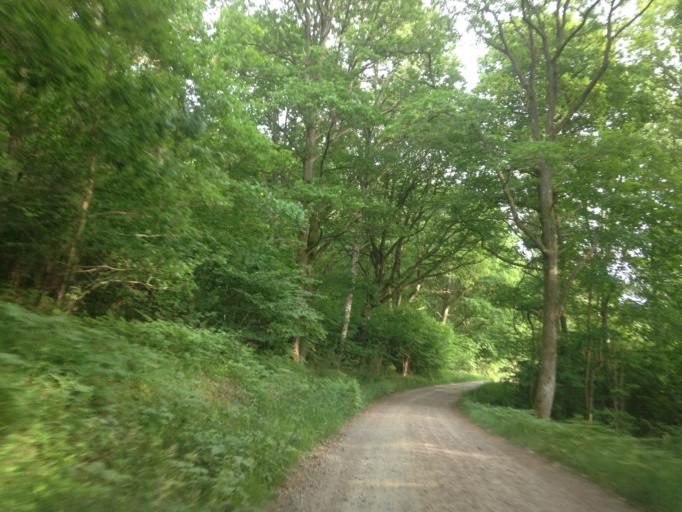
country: SE
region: Vaestra Goetaland
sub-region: Kungalvs Kommun
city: Kungalv
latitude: 57.8170
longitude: 11.9305
